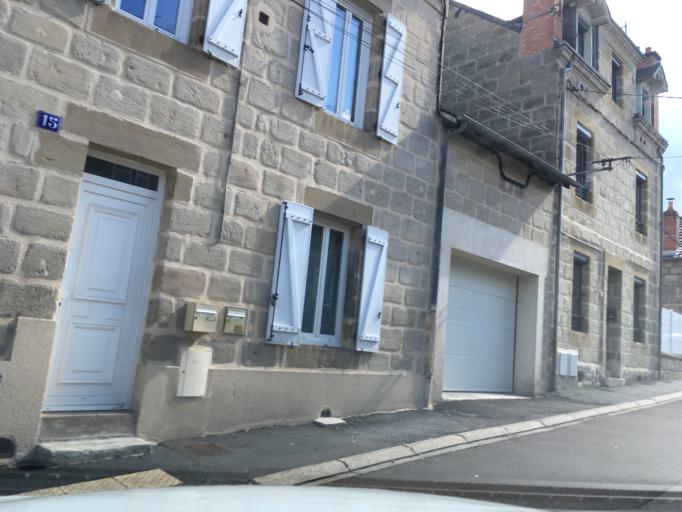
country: FR
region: Limousin
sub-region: Departement de la Correze
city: Brive-la-Gaillarde
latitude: 45.1521
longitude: 1.5337
